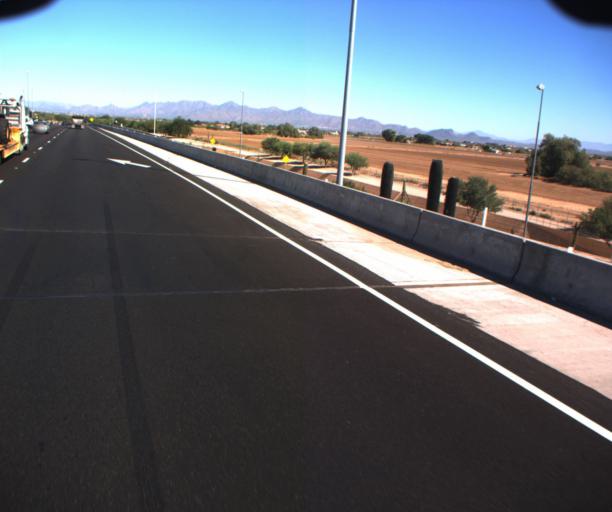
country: US
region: Arizona
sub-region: Maricopa County
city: Scottsdale
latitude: 33.4660
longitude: -111.8882
